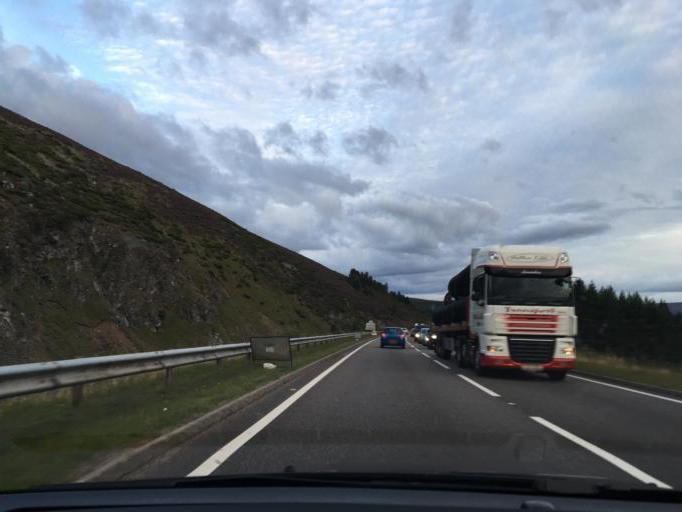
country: GB
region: Scotland
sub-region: Highland
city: Aviemore
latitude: 57.3024
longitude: -3.9275
